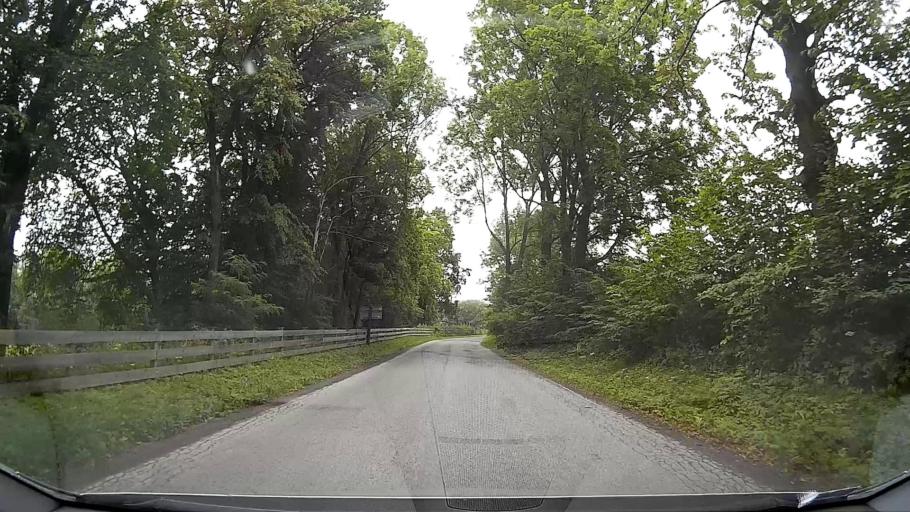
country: SK
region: Presovsky
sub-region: Okres Poprad
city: Poprad
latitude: 48.9906
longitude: 20.3822
